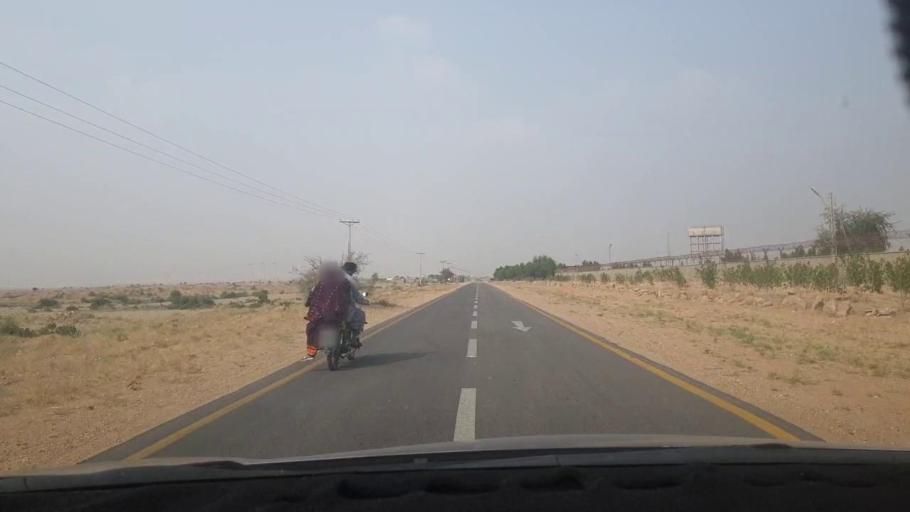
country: PK
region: Sindh
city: Jamshoro
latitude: 25.5582
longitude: 68.3192
